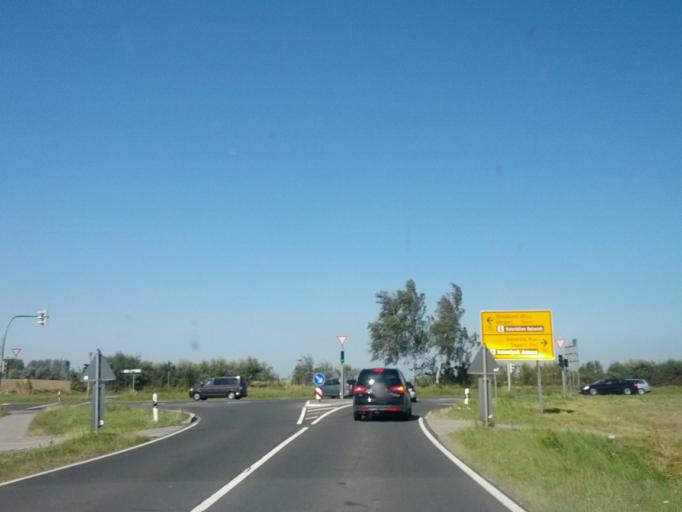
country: DE
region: Mecklenburg-Vorpommern
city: Sagard
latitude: 54.5094
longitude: 13.5361
